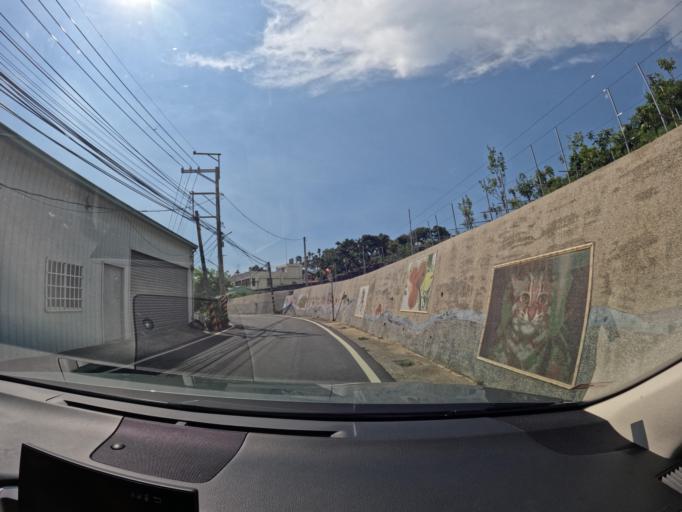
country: TW
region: Taiwan
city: Fengyuan
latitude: 24.3120
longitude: 120.7465
